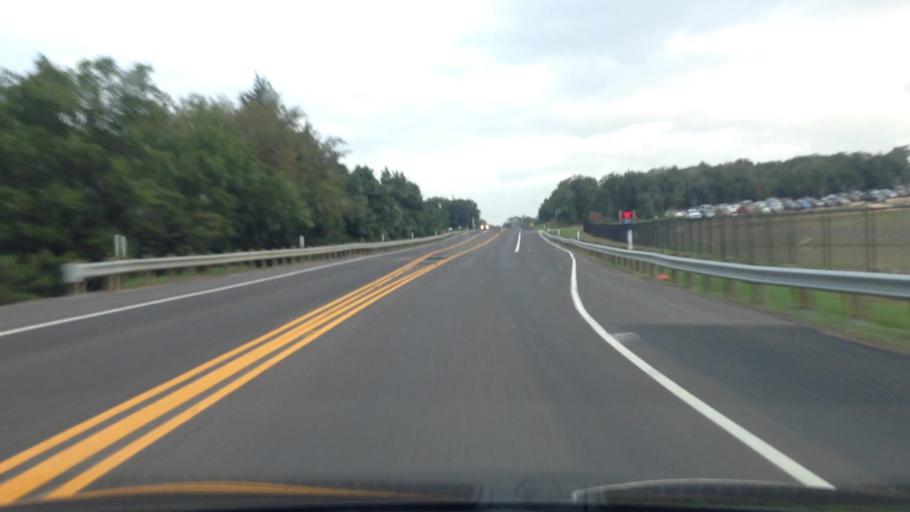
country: US
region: Texas
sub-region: Johnson County
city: Joshua
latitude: 32.4823
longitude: -97.3391
